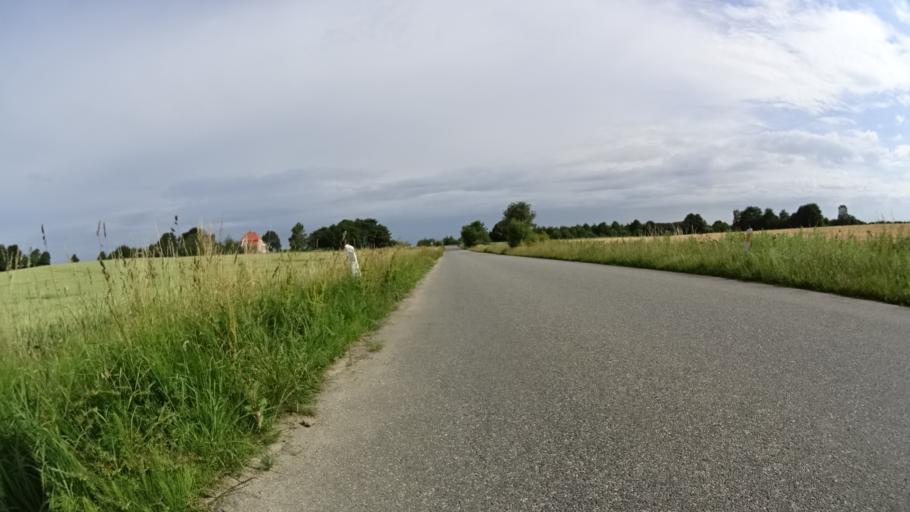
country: DK
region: Central Jutland
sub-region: Arhus Kommune
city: Kolt
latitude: 56.1274
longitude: 10.0800
